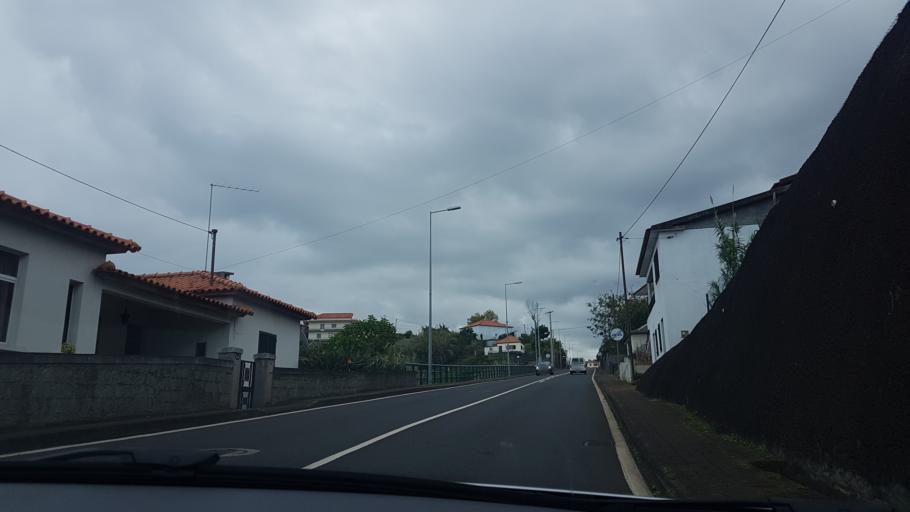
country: PT
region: Madeira
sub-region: Santana
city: Santana
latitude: 32.8210
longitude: -16.8881
